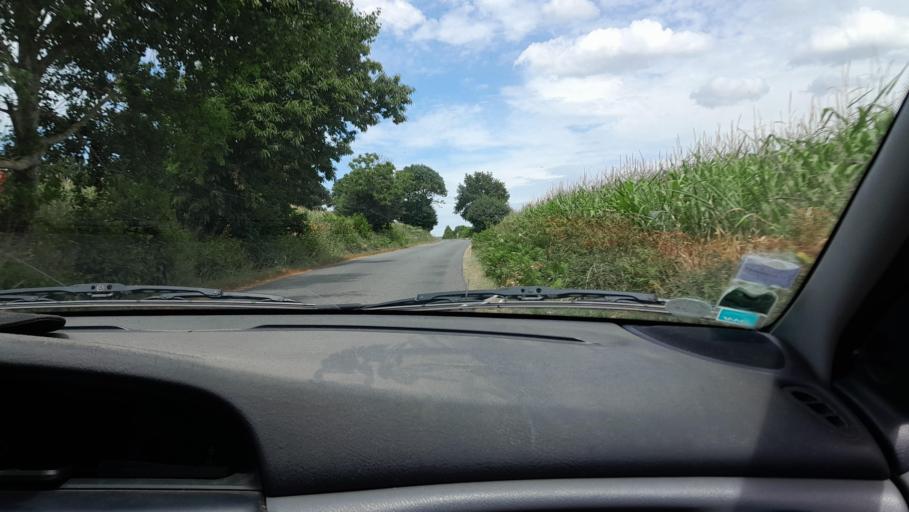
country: FR
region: Pays de la Loire
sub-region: Departement de la Mayenne
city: Juvigne
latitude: 48.1899
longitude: -1.0307
